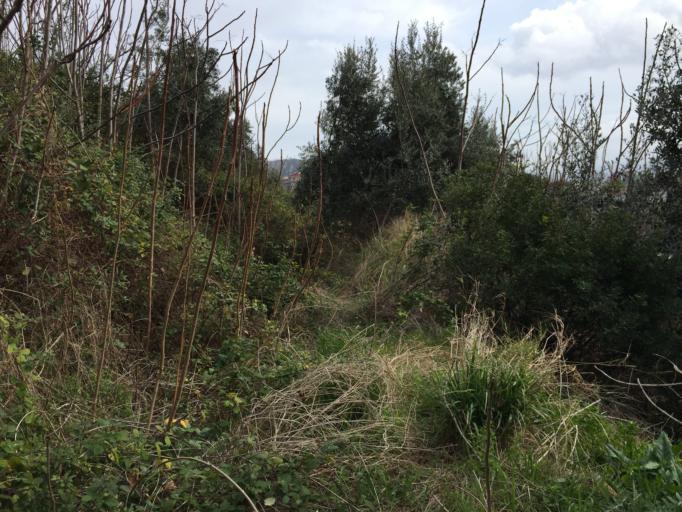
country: IT
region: Campania
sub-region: Provincia di Napoli
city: Pozzuoli
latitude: 40.8329
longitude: 14.1290
